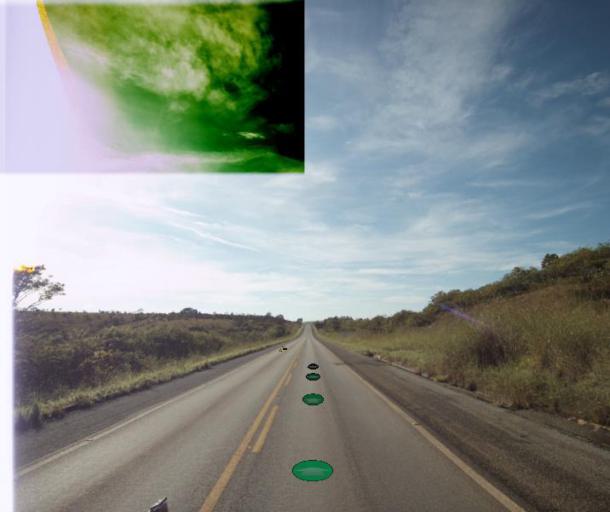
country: BR
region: Goias
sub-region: Pirenopolis
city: Pirenopolis
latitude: -15.7805
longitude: -48.4932
